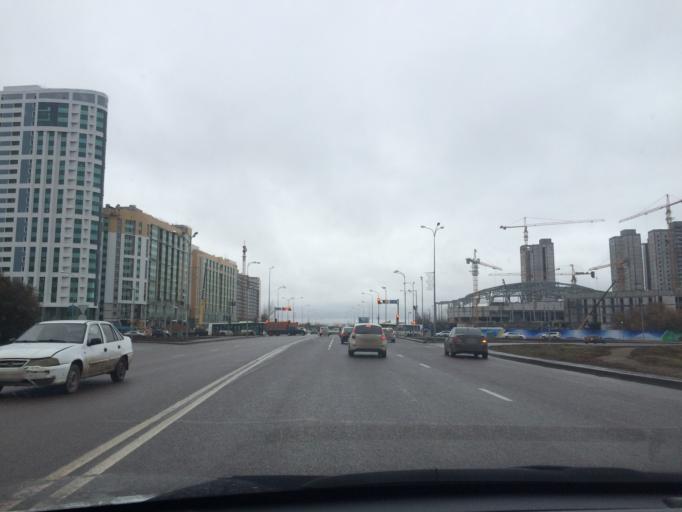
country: KZ
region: Astana Qalasy
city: Astana
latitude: 51.1172
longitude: 71.4118
